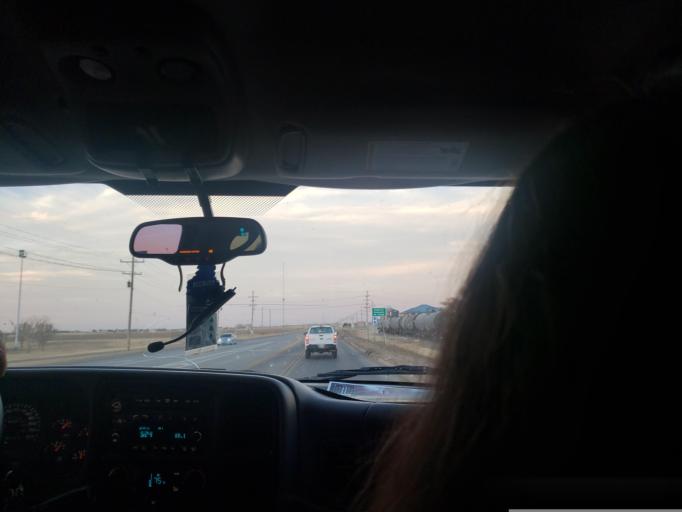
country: US
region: Kansas
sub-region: Seward County
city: Liberal
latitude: 37.0519
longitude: -100.9044
